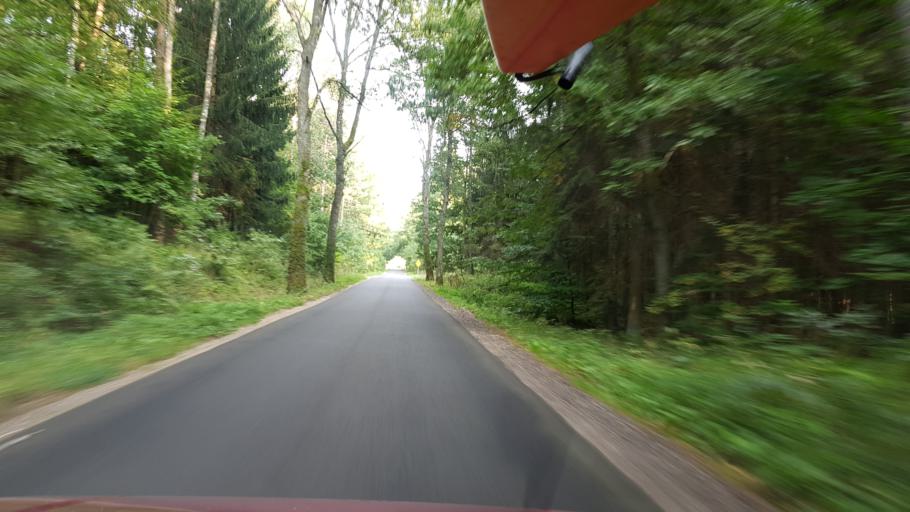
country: PL
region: West Pomeranian Voivodeship
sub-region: Powiat szczecinecki
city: Bialy Bor
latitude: 54.0210
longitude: 16.8525
